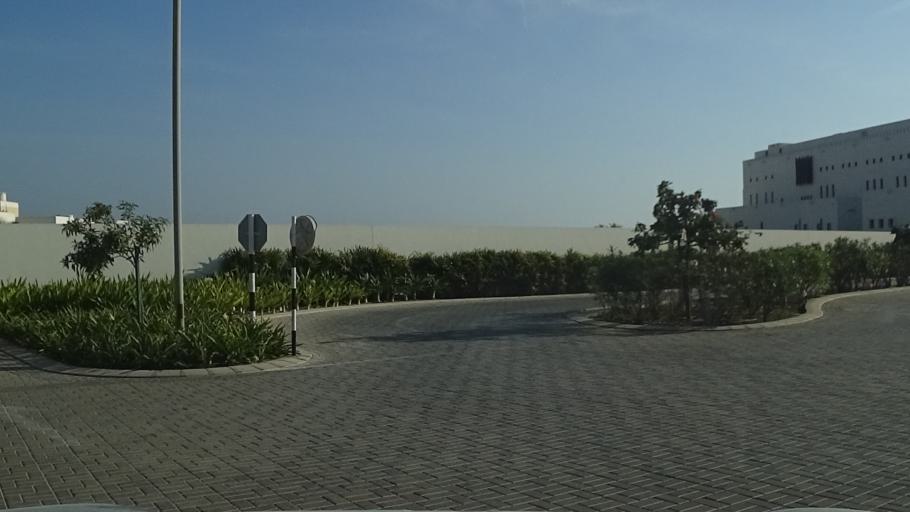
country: OM
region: Zufar
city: Salalah
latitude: 17.0088
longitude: 54.1447
